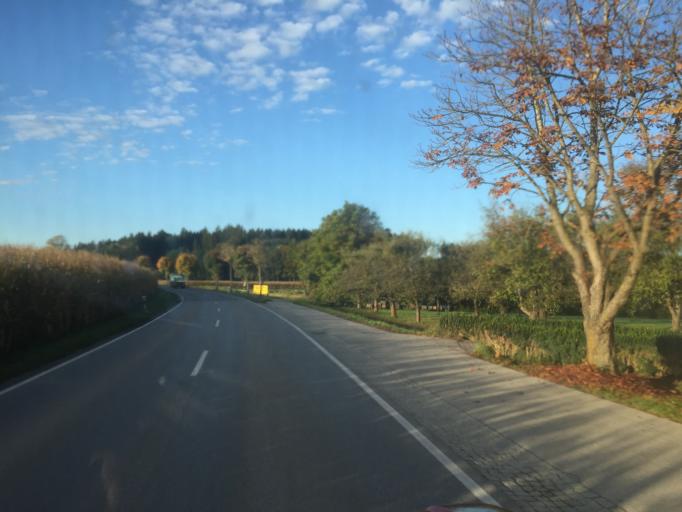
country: DE
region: Bavaria
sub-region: Upper Bavaria
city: Chieming
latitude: 47.9098
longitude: 12.5584
